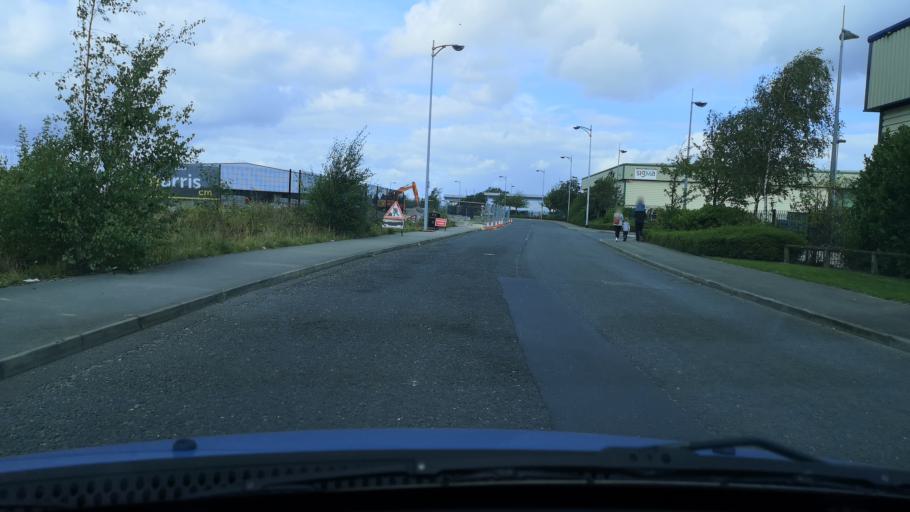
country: GB
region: England
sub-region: City and Borough of Wakefield
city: Castleford
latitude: 53.7109
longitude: -1.3469
